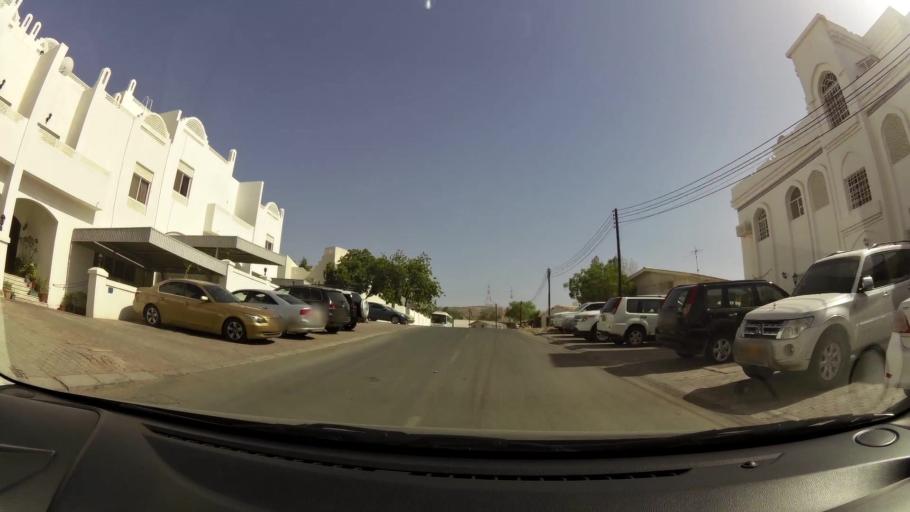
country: OM
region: Muhafazat Masqat
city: Muscat
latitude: 23.6046
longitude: 58.4949
